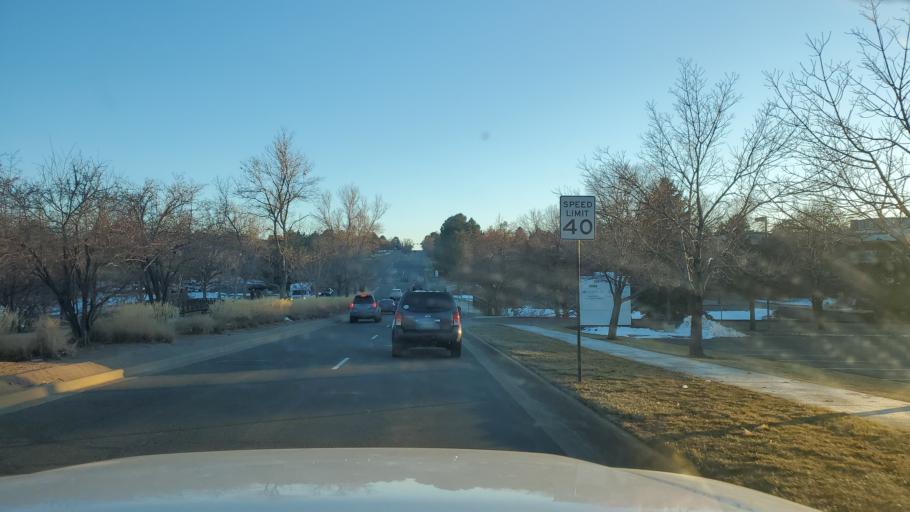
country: US
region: Colorado
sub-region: Arapahoe County
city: Castlewood
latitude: 39.6083
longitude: -104.9042
